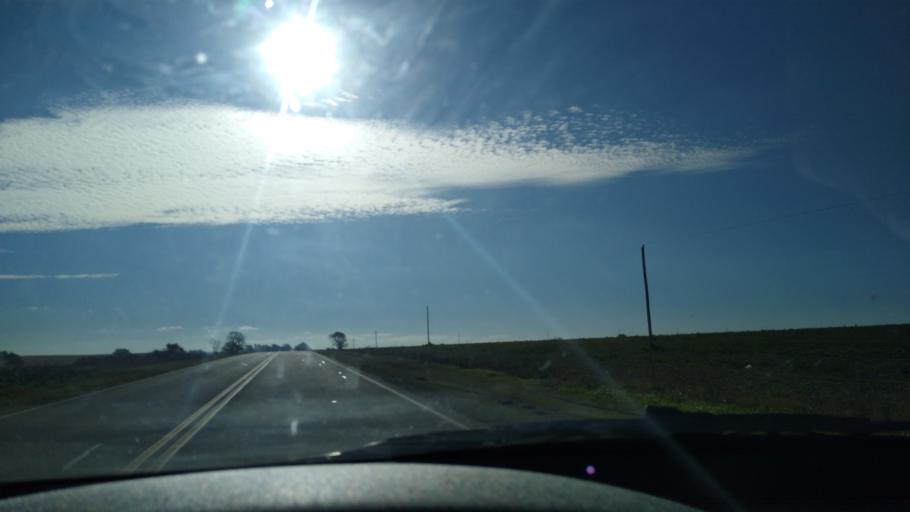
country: AR
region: Entre Rios
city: Aranguren
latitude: -32.3473
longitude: -60.3668
